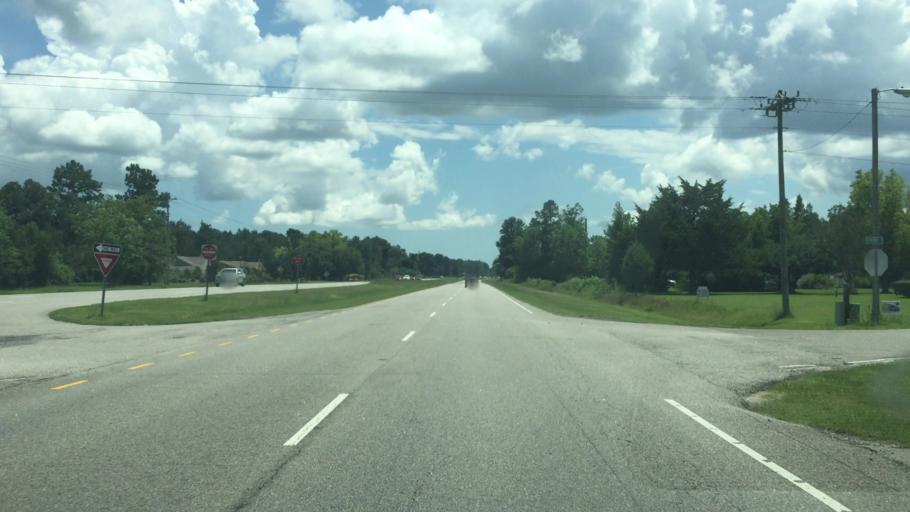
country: US
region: South Carolina
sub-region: Horry County
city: Loris
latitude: 33.9939
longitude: -78.7503
